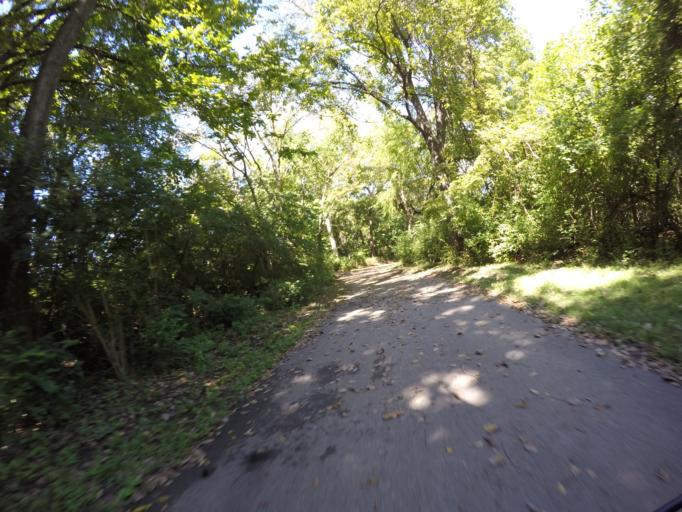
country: US
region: Kansas
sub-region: Johnson County
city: Overland Park
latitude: 38.9393
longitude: -94.6610
